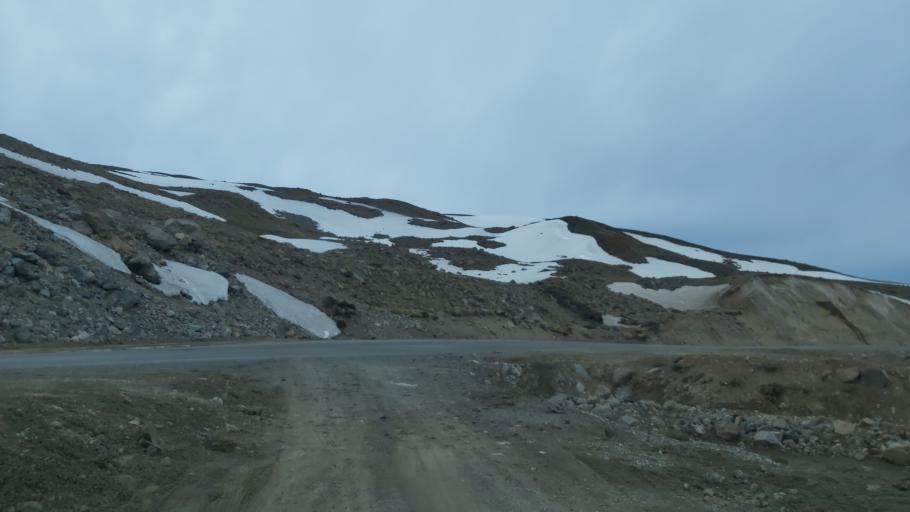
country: CL
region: Maule
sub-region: Provincia de Linares
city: Colbun
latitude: -35.9913
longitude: -70.5586
